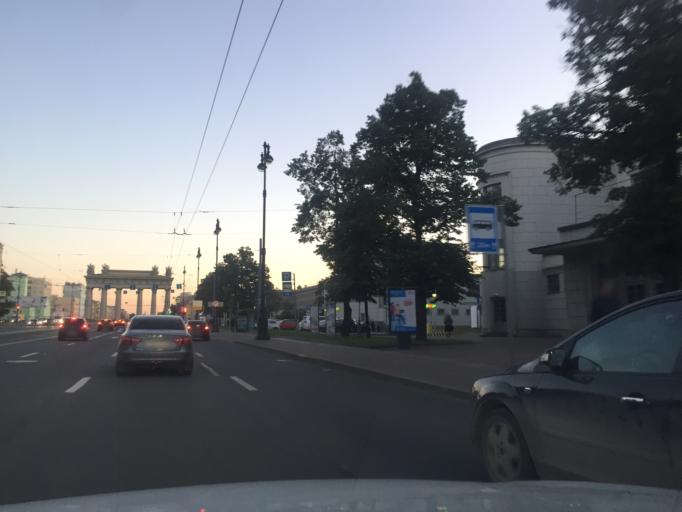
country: RU
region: St.-Petersburg
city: Admiralteisky
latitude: 59.8941
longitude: 30.3191
